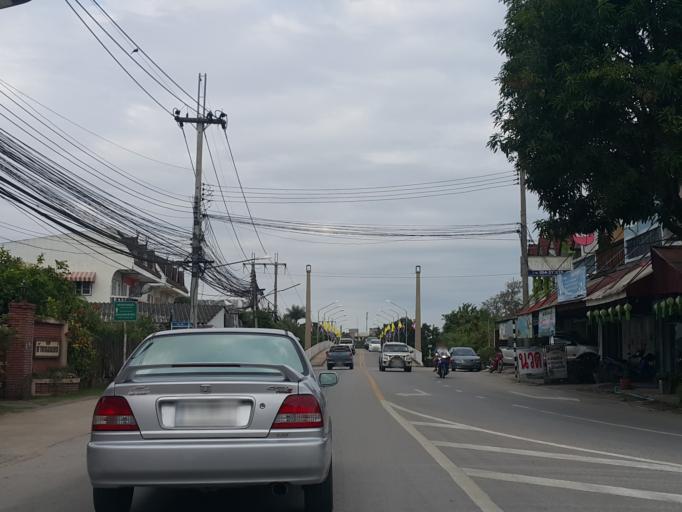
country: TH
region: Lampang
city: Lampang
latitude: 18.2930
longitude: 99.4886
